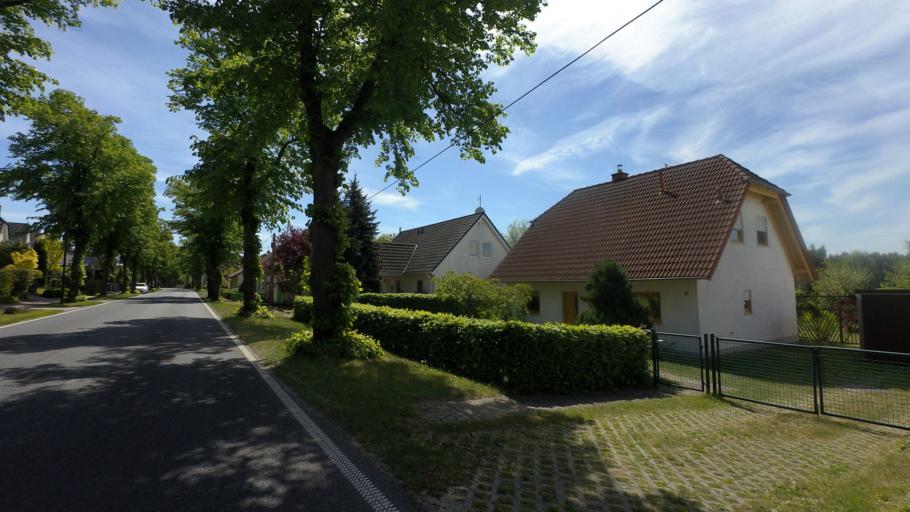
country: DE
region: Brandenburg
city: Luckenwalde
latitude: 52.1376
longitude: 13.1221
